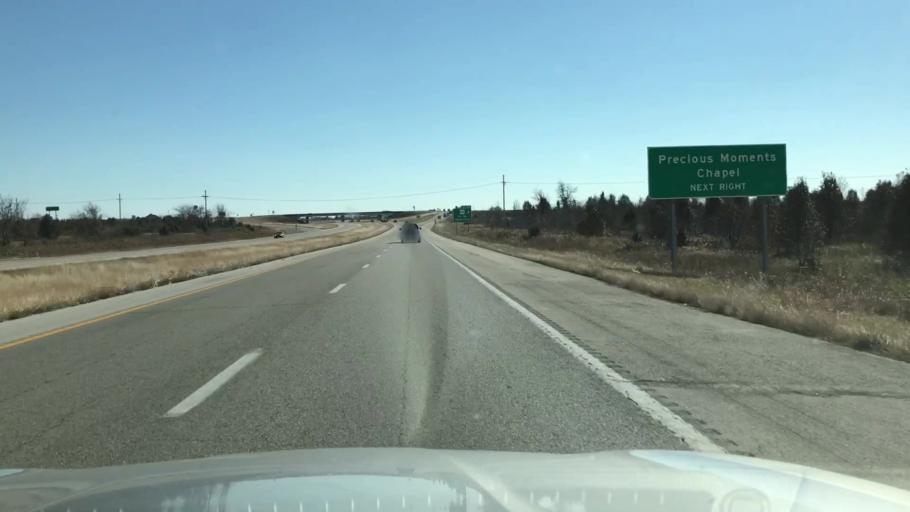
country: US
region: Missouri
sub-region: Jasper County
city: Carthage
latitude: 37.1458
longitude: -94.3268
